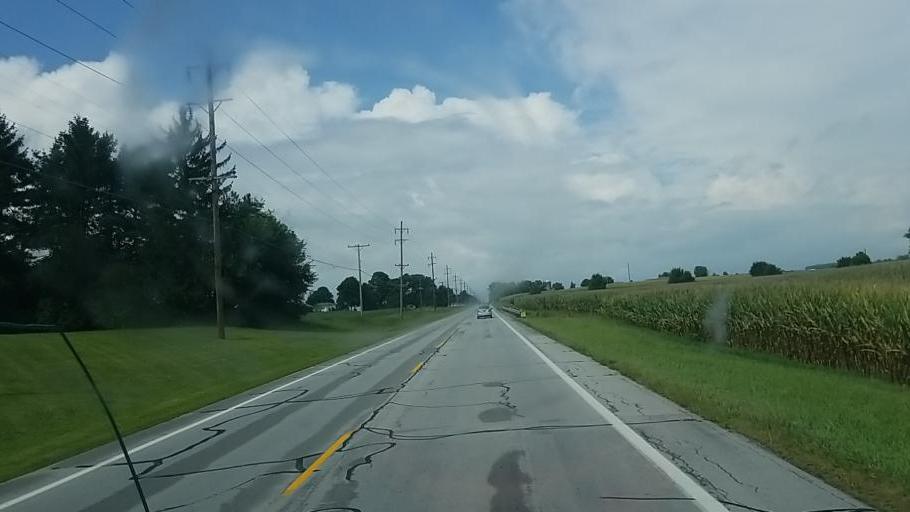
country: US
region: Ohio
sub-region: Champaign County
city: Urbana
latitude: 40.1657
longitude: -83.7447
